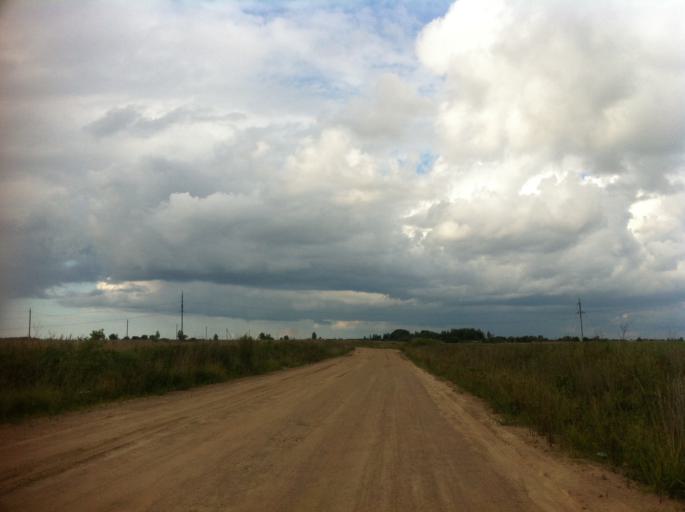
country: RU
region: Pskov
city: Izborsk
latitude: 57.8273
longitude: 27.9816
